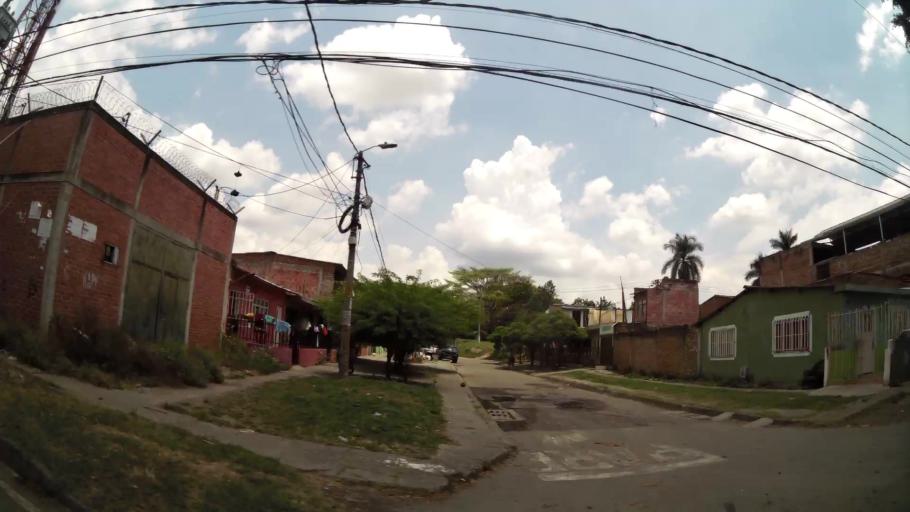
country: CO
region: Valle del Cauca
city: Cali
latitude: 3.4615
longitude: -76.4789
